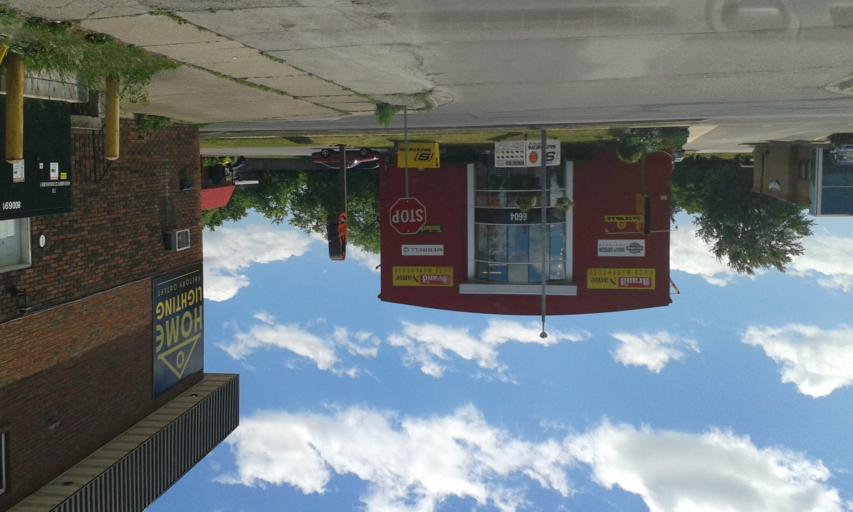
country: CA
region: Ontario
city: Niagara Falls
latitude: 43.0897
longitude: -79.1051
